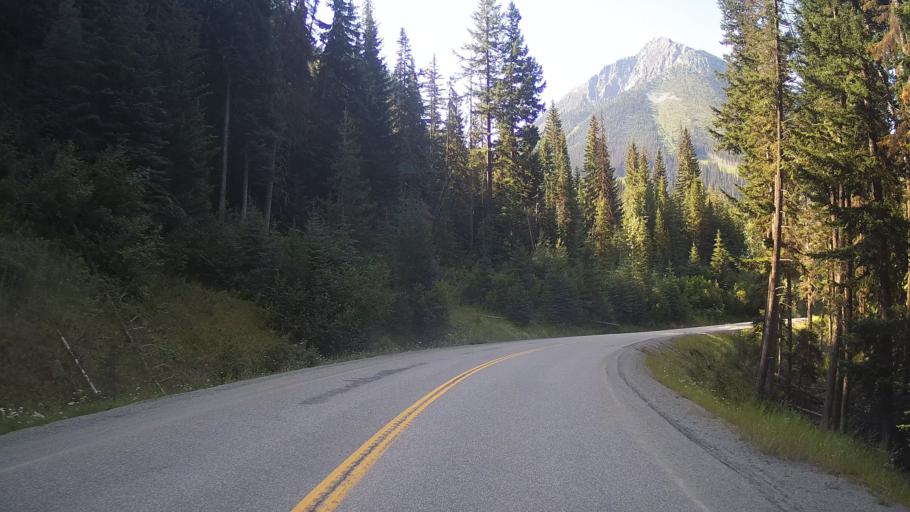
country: CA
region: British Columbia
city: Lillooet
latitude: 50.4369
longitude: -122.2522
